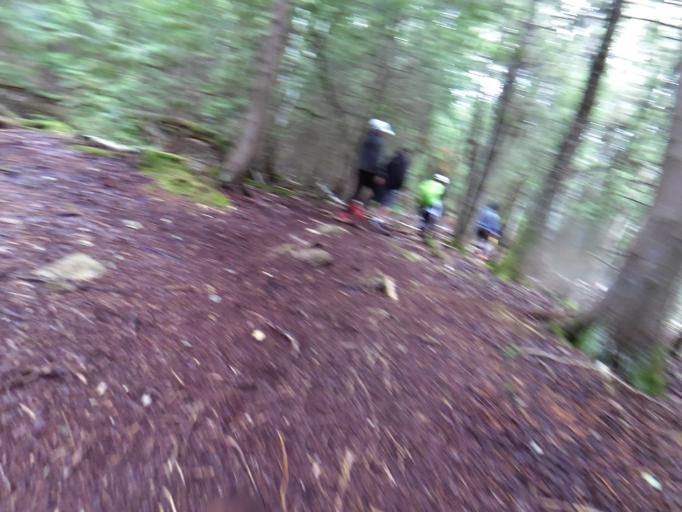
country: CA
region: Ontario
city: Tobermory
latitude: 45.2610
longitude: -81.6425
